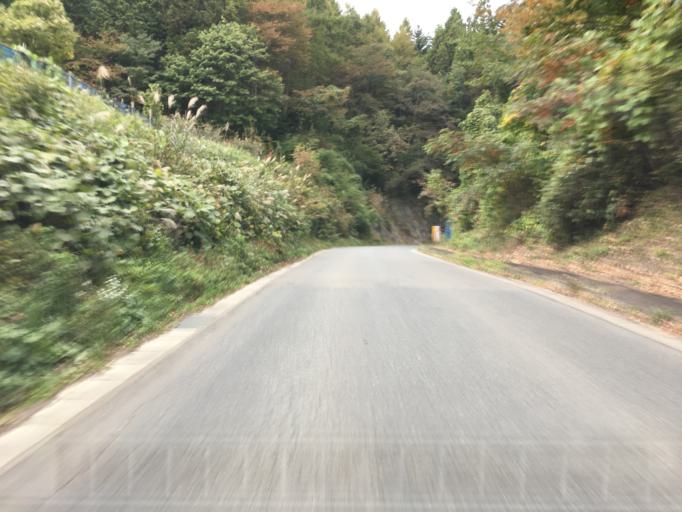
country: JP
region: Fukushima
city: Yanagawamachi-saiwaicho
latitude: 37.7702
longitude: 140.7146
